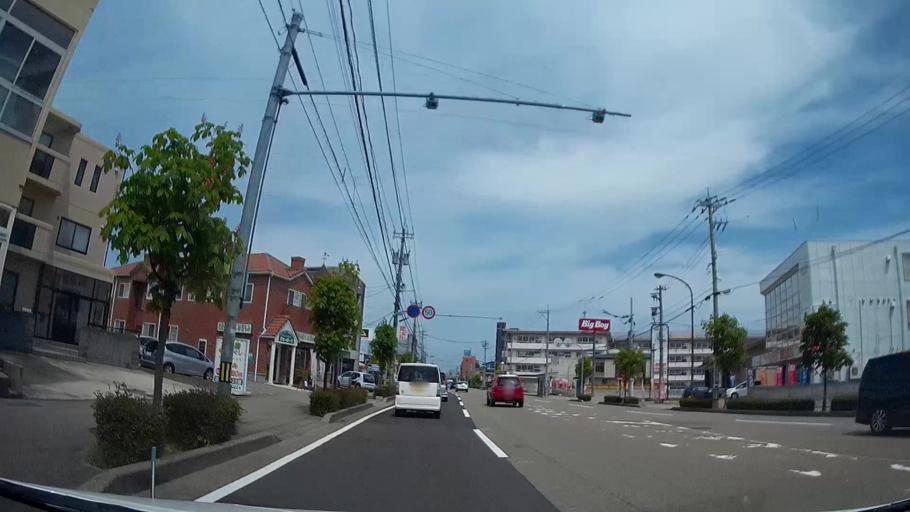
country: JP
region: Ishikawa
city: Kanazawa-shi
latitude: 36.5871
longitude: 136.6480
